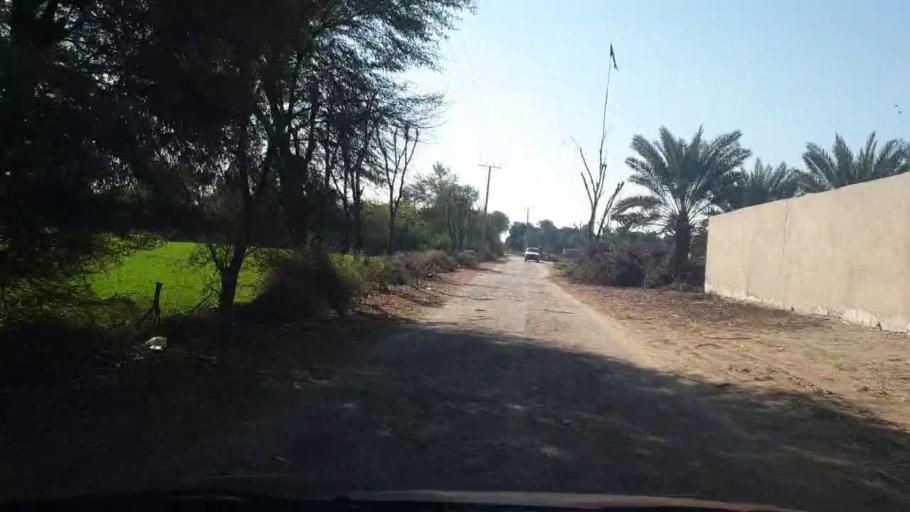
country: PK
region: Sindh
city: Bozdar
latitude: 27.2609
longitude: 68.6529
